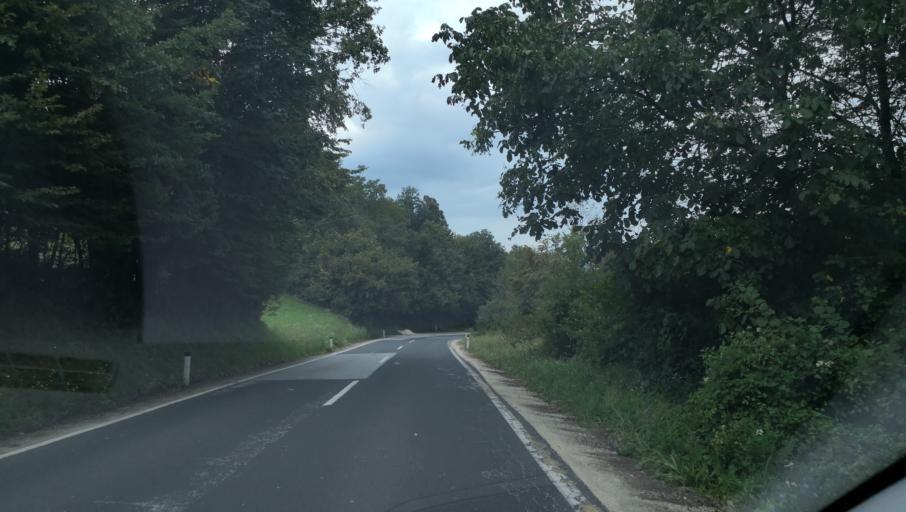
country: SI
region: Novo Mesto
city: Novo Mesto
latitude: 45.7450
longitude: 15.2092
